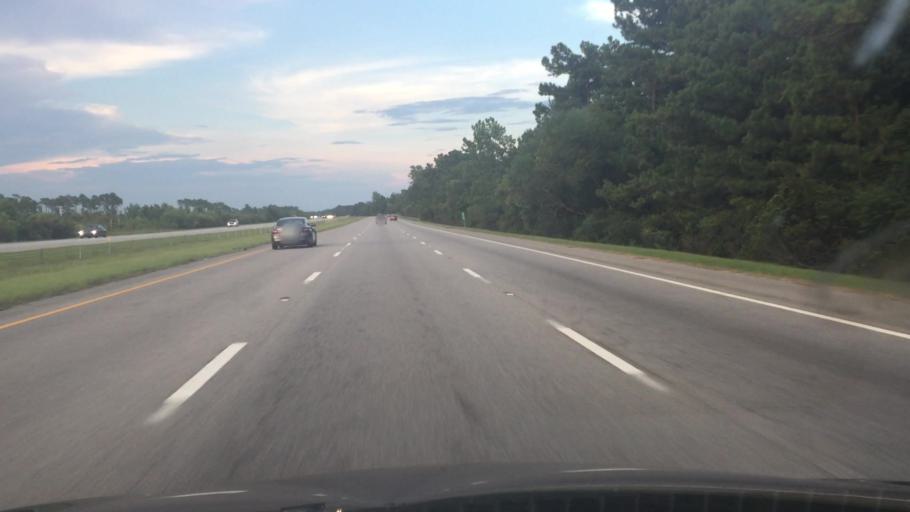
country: US
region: South Carolina
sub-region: Horry County
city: Myrtle Beach
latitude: 33.7685
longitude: -78.8276
